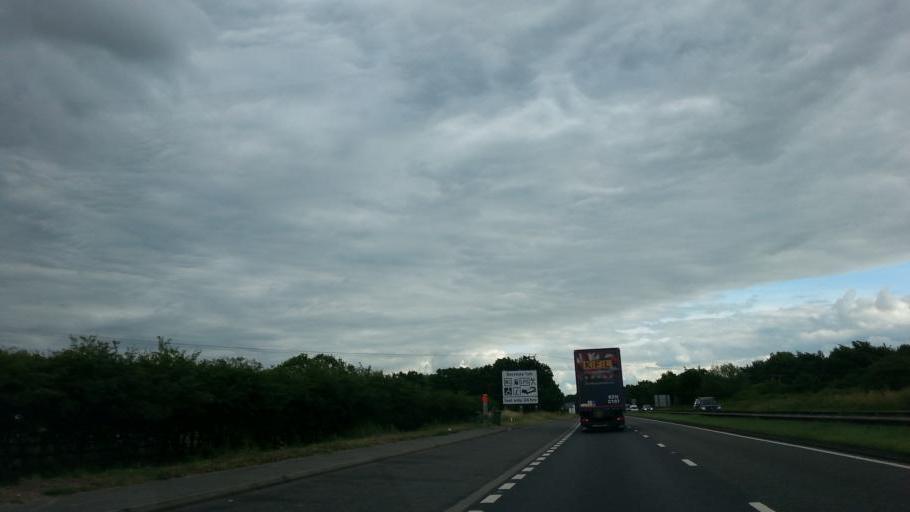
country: GB
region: England
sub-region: Nottinghamshire
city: Retford
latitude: 53.2649
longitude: -0.9451
